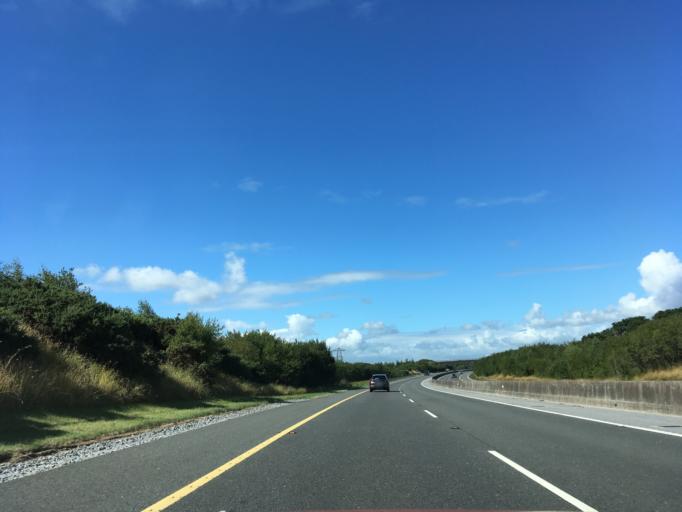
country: IE
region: Munster
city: Cahir
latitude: 52.3332
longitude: -8.0333
